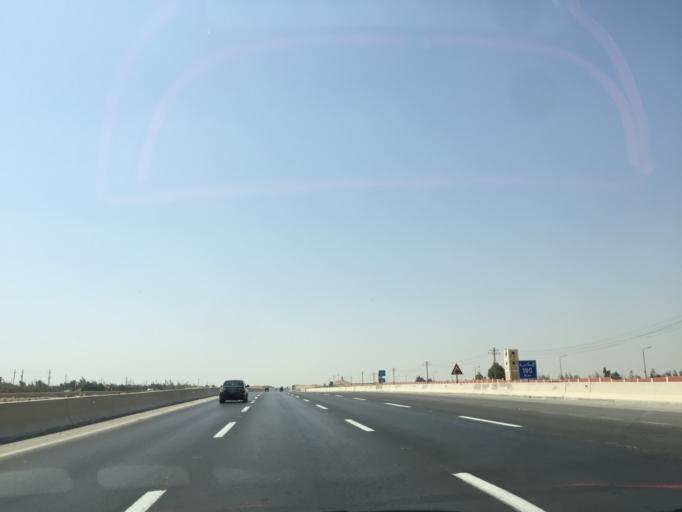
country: EG
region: Al Jizah
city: Awsim
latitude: 30.0847
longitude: 30.9883
